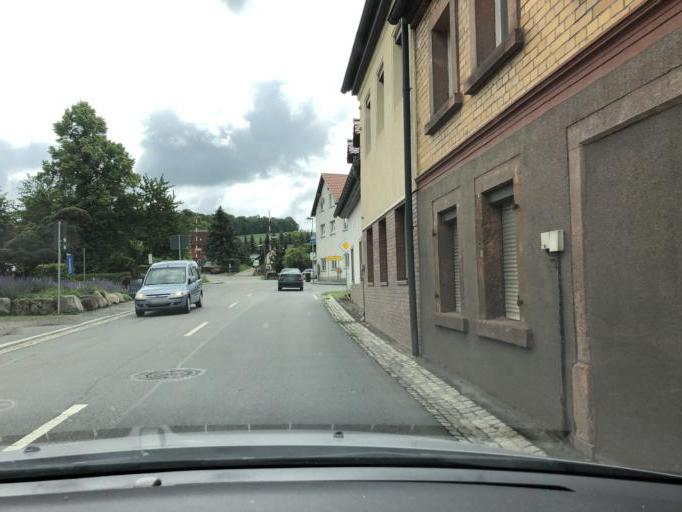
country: DE
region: Saxony
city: Waldenburg
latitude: 50.8673
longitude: 12.6139
